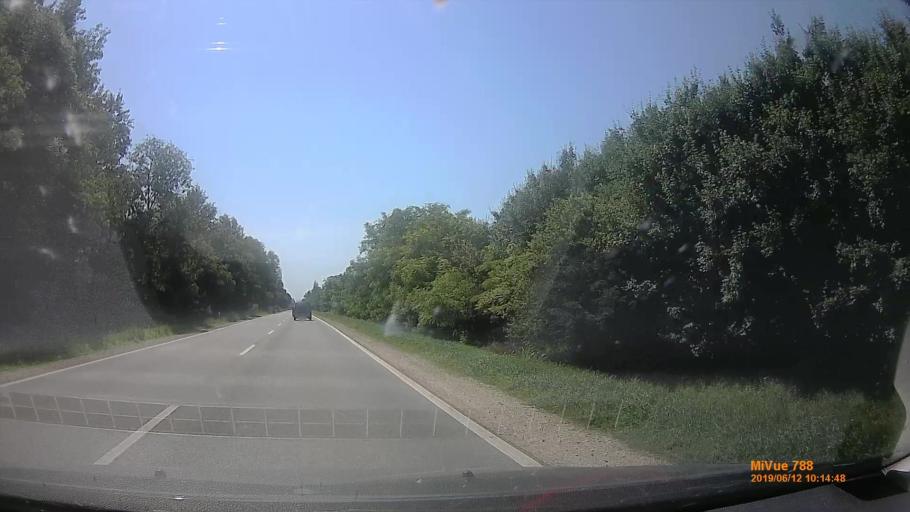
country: HU
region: Pest
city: Dabas
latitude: 47.2092
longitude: 19.2862
